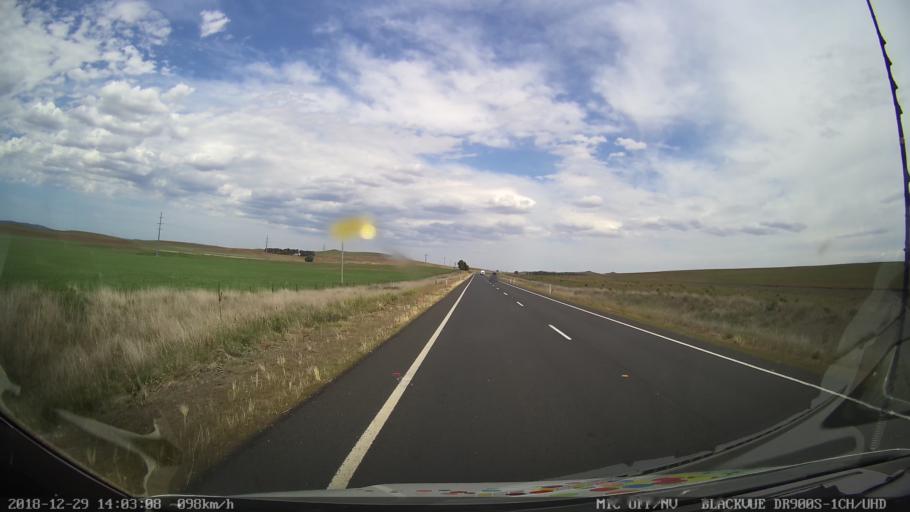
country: AU
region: New South Wales
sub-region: Cooma-Monaro
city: Cooma
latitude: -36.2973
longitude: 149.1815
